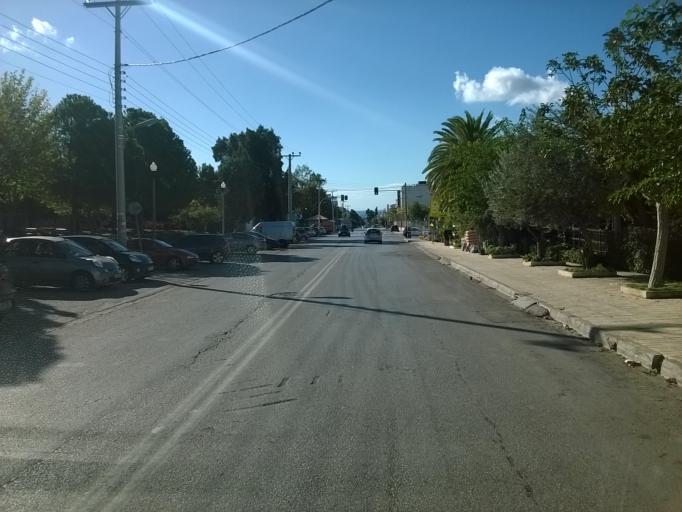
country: GR
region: Attica
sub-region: Nomarchia Athinas
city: Argyroupoli
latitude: 37.8857
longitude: 23.7601
